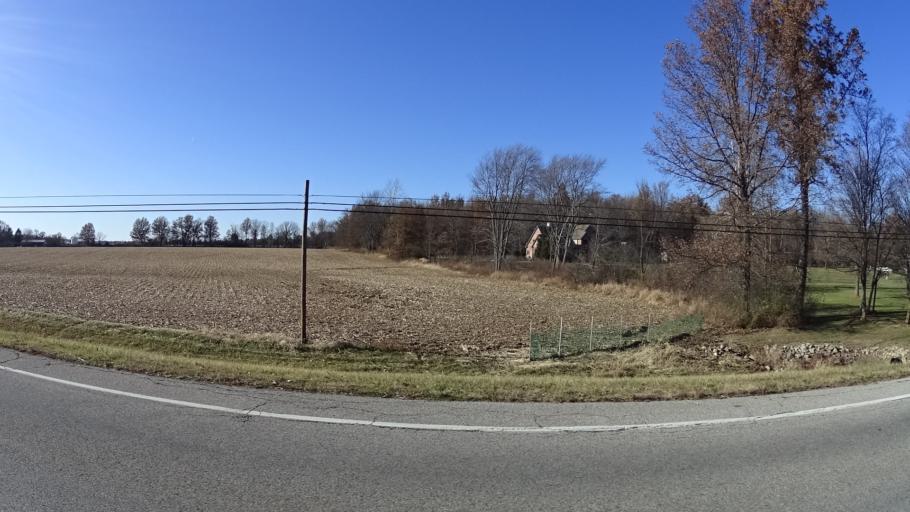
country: US
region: Ohio
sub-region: Lorain County
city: Elyria
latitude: 41.3154
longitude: -82.1420
